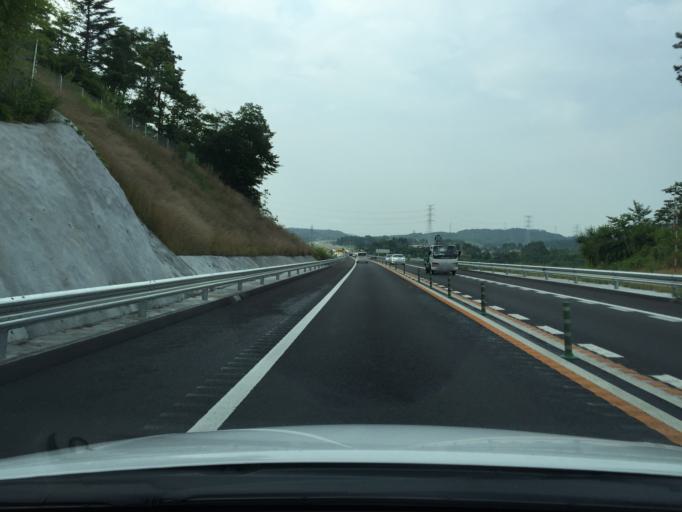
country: JP
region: Fukushima
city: Namie
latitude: 37.3927
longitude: 140.9663
